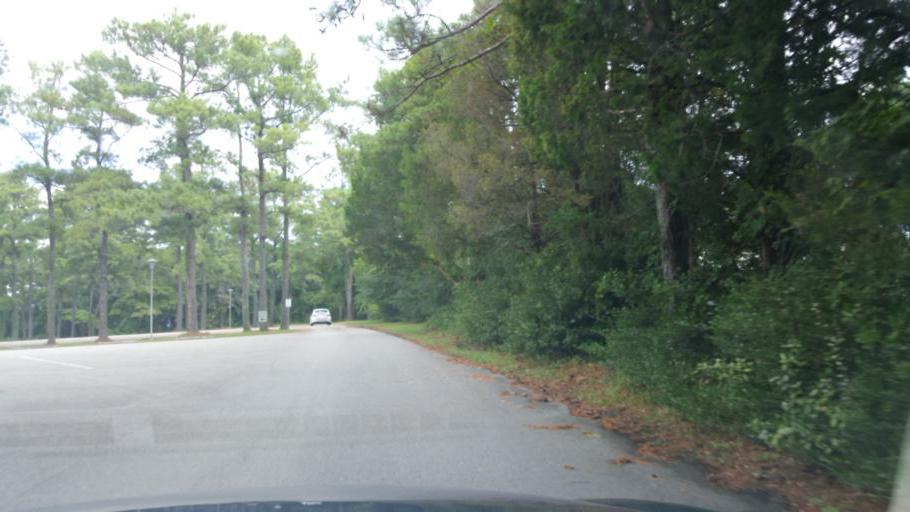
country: US
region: North Carolina
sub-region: Dare County
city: Manteo
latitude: 35.9370
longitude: -75.7066
